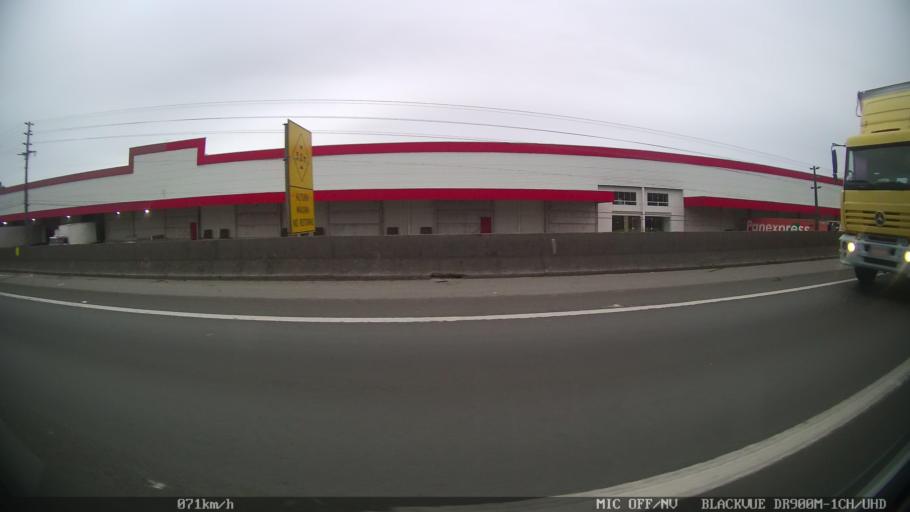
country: BR
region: Santa Catarina
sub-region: Penha
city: Penha
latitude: -26.7128
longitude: -48.7035
